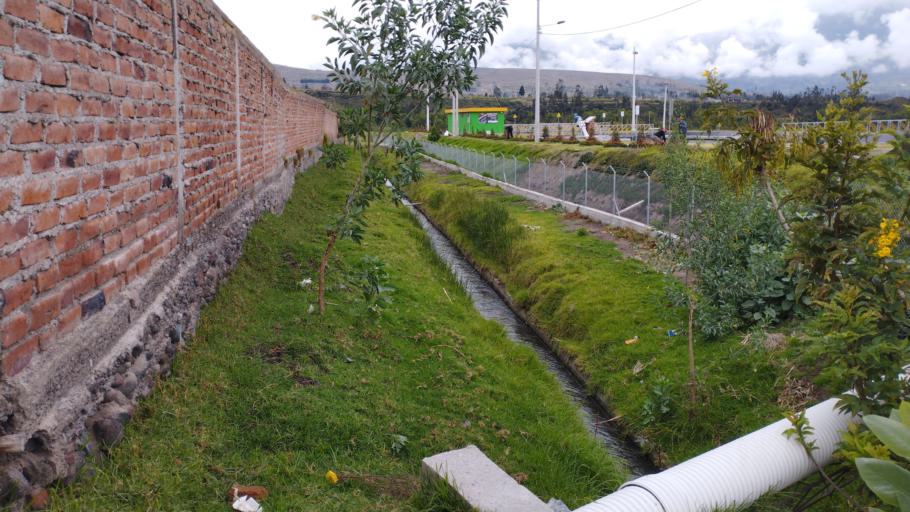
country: EC
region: Chimborazo
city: Guano
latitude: -1.6131
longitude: -78.6080
